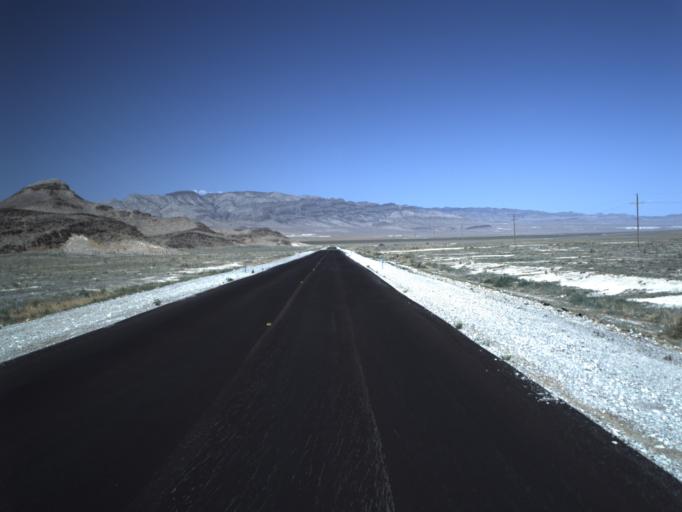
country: US
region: Utah
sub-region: Beaver County
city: Milford
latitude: 39.0538
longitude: -113.4255
